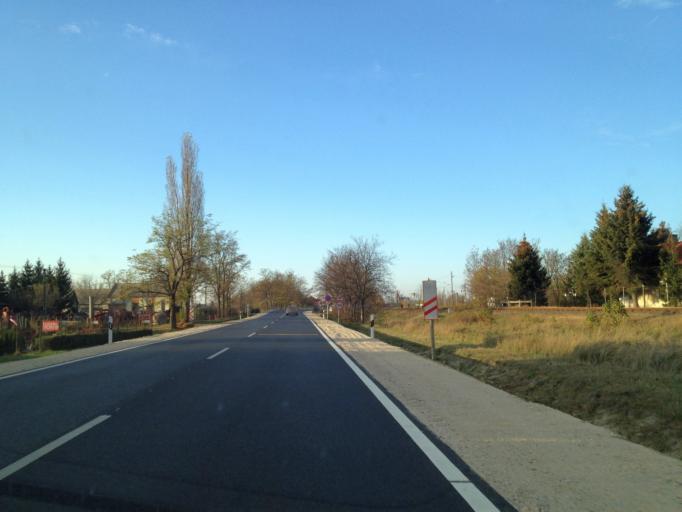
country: HU
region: Gyor-Moson-Sopron
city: Gyorujbarat
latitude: 47.6411
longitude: 17.6641
